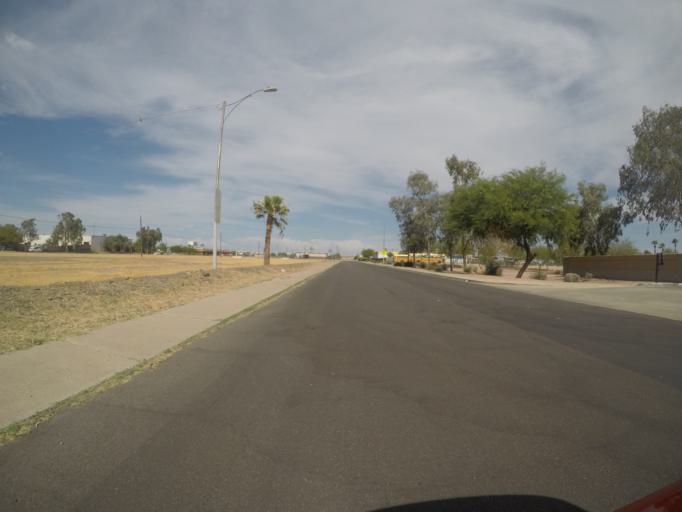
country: US
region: Arizona
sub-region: Maricopa County
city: Phoenix
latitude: 33.4323
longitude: -112.0514
